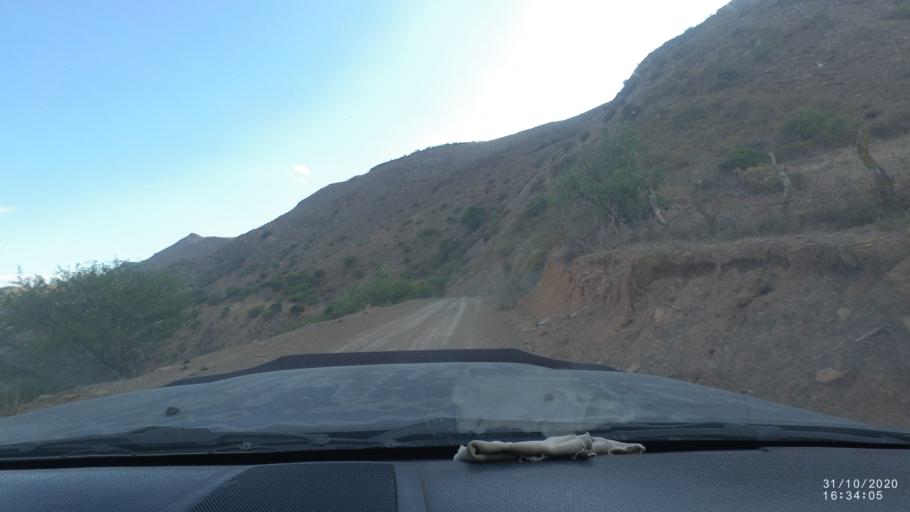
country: BO
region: Chuquisaca
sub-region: Provincia Zudanez
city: Mojocoya
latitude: -18.4462
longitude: -64.5841
